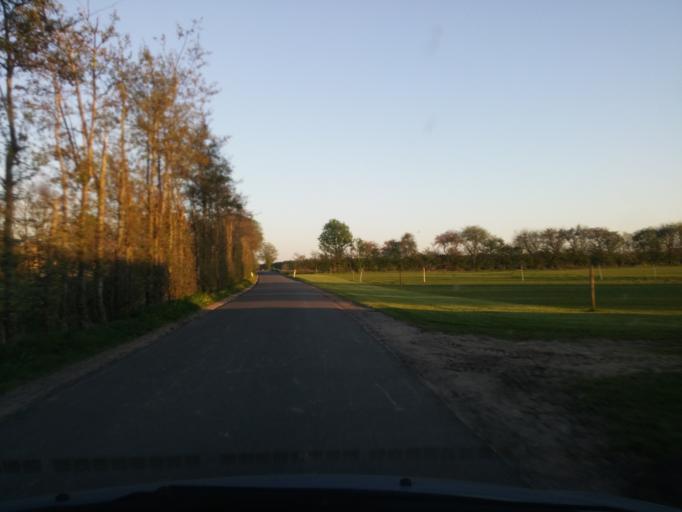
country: DK
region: South Denmark
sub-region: Nyborg Kommune
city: Ullerslev
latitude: 55.3855
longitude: 10.6394
